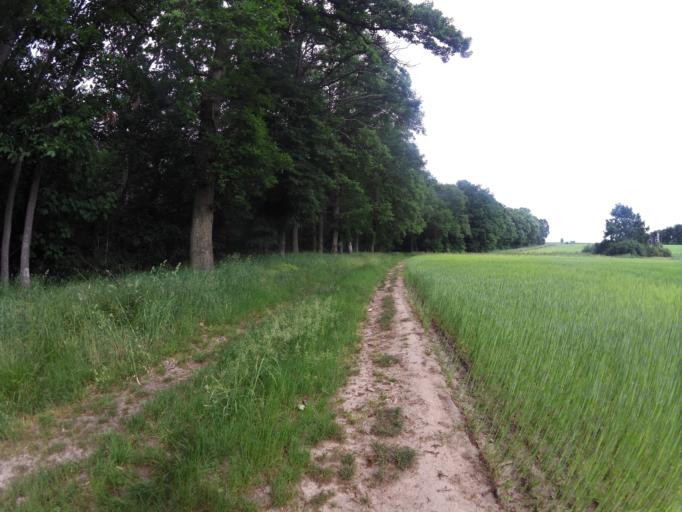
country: DE
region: Bavaria
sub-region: Regierungsbezirk Unterfranken
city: Frickenhausen
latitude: 49.6946
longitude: 10.0753
